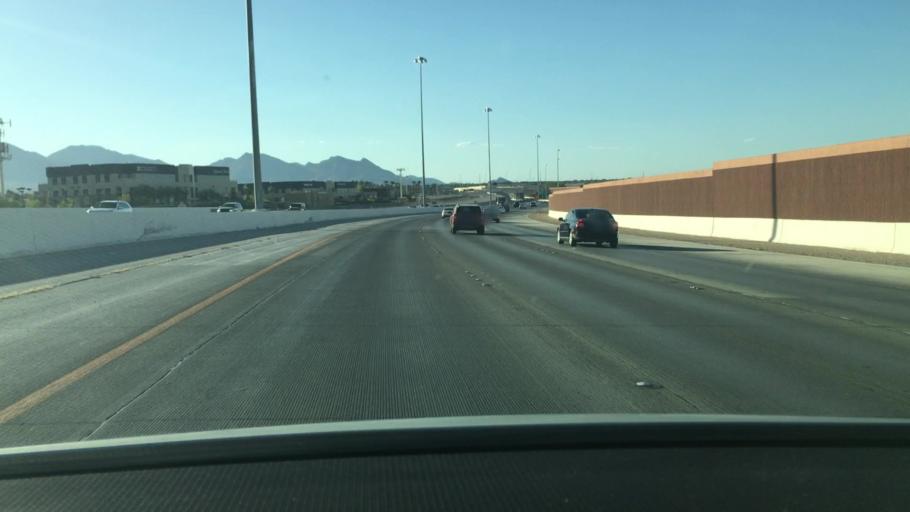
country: US
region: Nevada
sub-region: Clark County
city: Summerlin South
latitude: 36.1008
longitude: -115.2942
